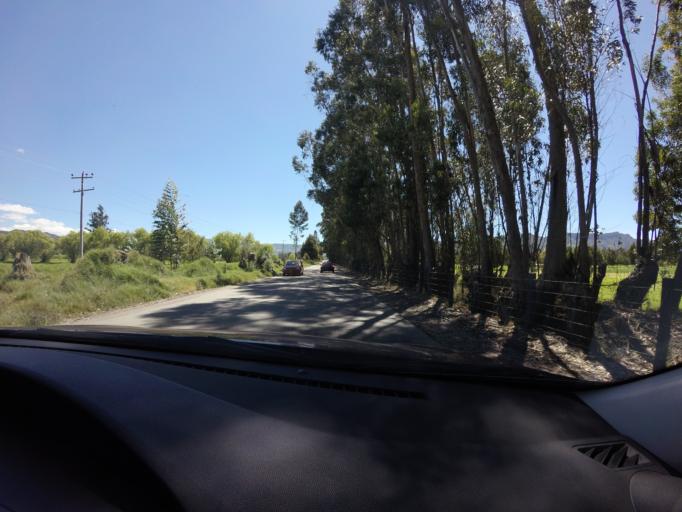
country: CO
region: Cundinamarca
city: Ubate
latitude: 5.2908
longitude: -73.8102
